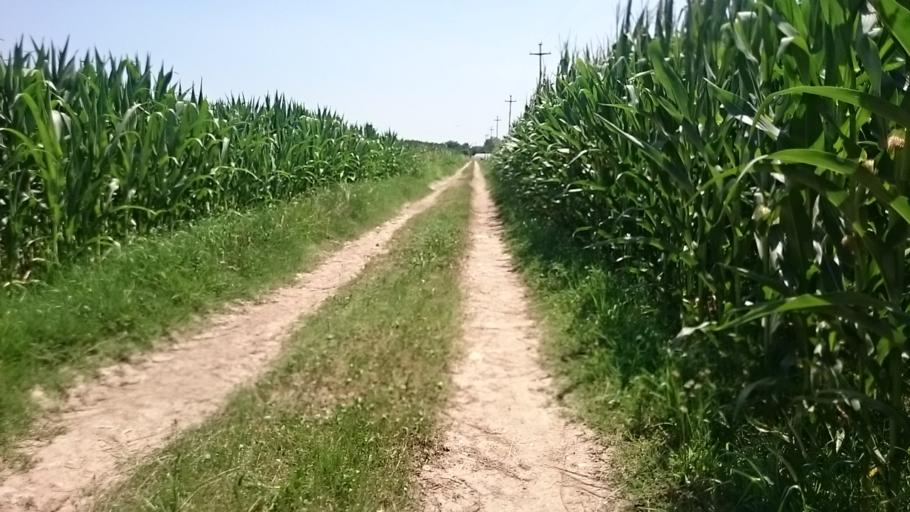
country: IT
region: Veneto
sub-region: Provincia di Vicenza
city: Vicenza
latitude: 45.5337
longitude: 11.5654
